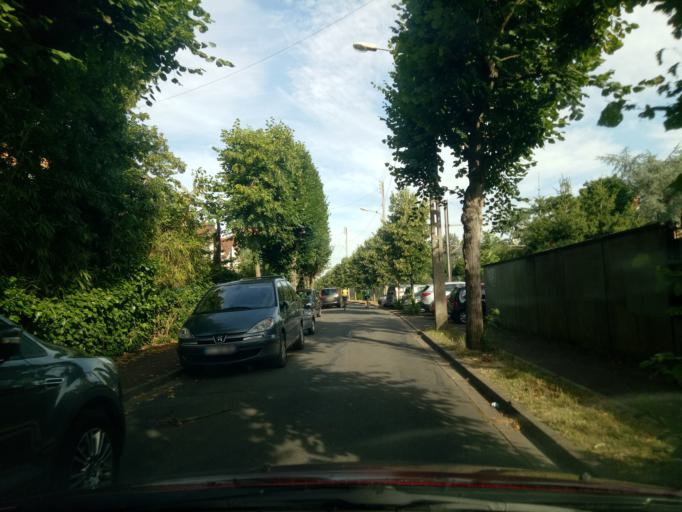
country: FR
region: Ile-de-France
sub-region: Departement des Yvelines
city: Chatou
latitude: 48.8857
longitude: 2.1493
